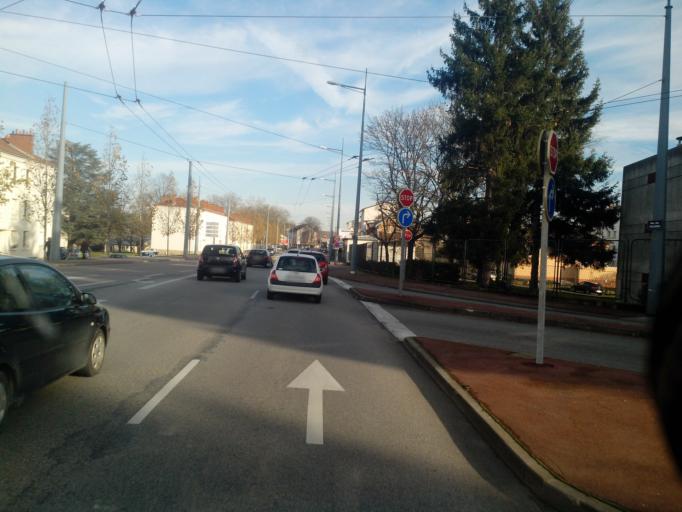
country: FR
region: Limousin
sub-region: Departement de la Haute-Vienne
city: Limoges
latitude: 45.8524
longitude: 1.2549
